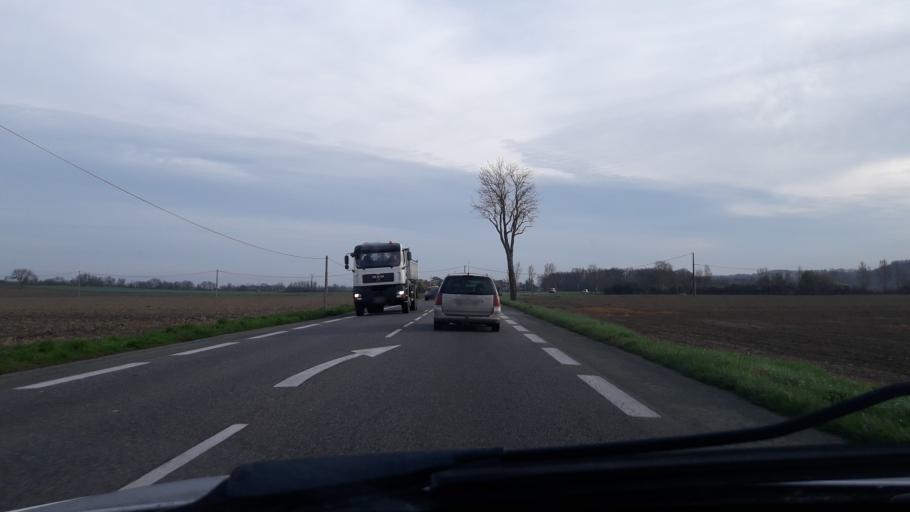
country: FR
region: Midi-Pyrenees
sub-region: Departement de la Haute-Garonne
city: Rieux-Volvestre
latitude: 43.2711
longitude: 1.1986
